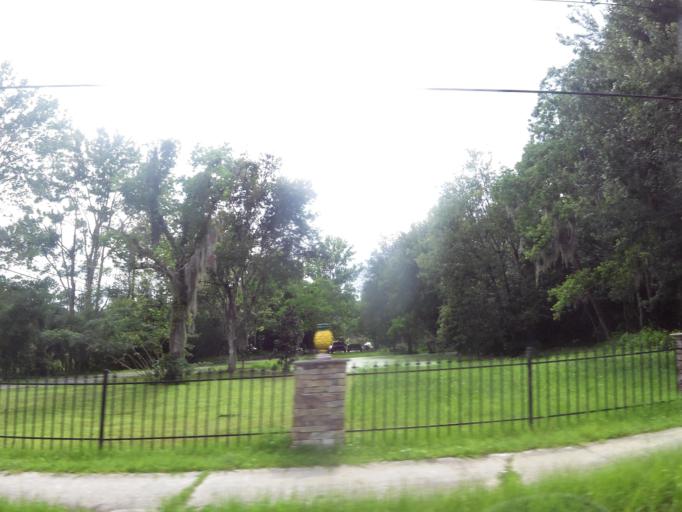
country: US
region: Florida
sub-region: Duval County
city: Jacksonville
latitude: 30.3026
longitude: -81.5309
